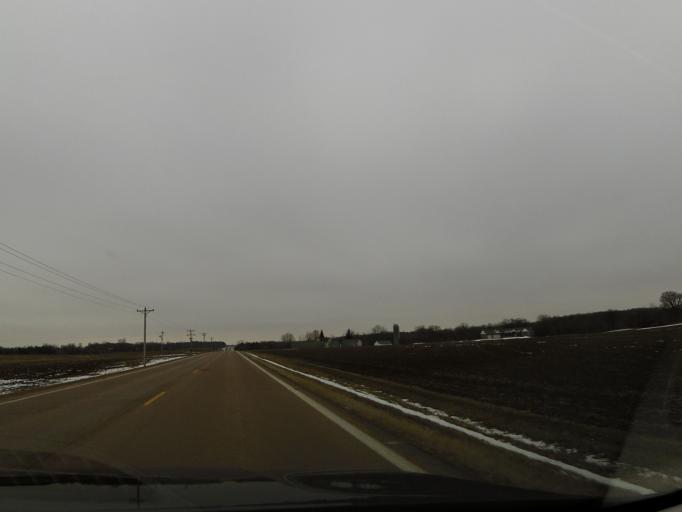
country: US
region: Minnesota
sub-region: Carver County
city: Carver
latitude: 44.7492
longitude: -93.6840
